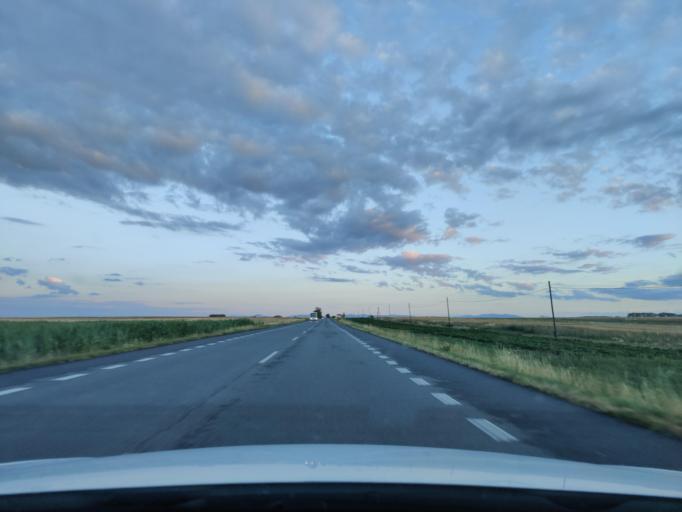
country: PL
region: Opole Voivodeship
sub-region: Powiat nyski
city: Skoroszyce
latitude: 50.5912
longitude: 17.3820
